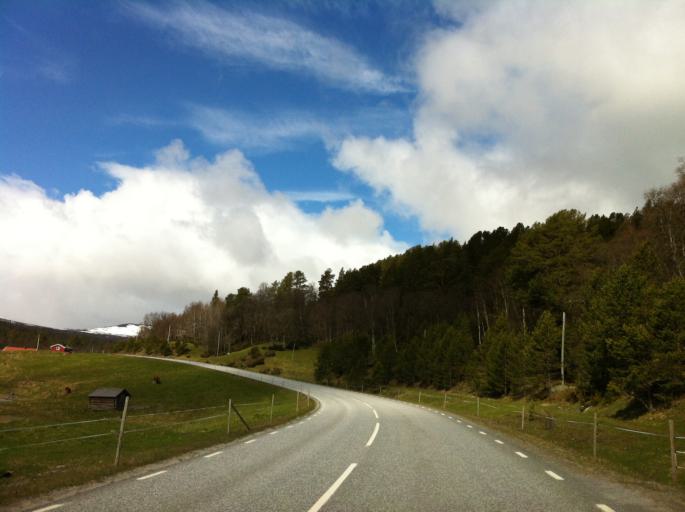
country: NO
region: Sor-Trondelag
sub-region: Tydal
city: Aas
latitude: 62.6120
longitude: 12.4997
